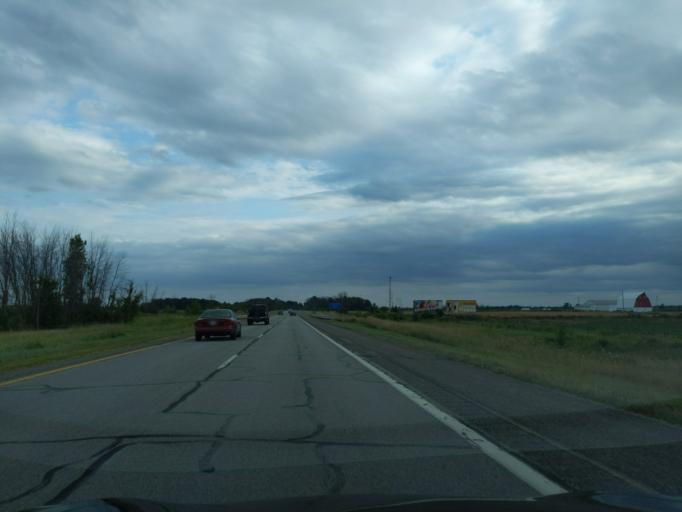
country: US
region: Michigan
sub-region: Isabella County
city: Mount Pleasant
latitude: 43.6851
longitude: -84.7576
